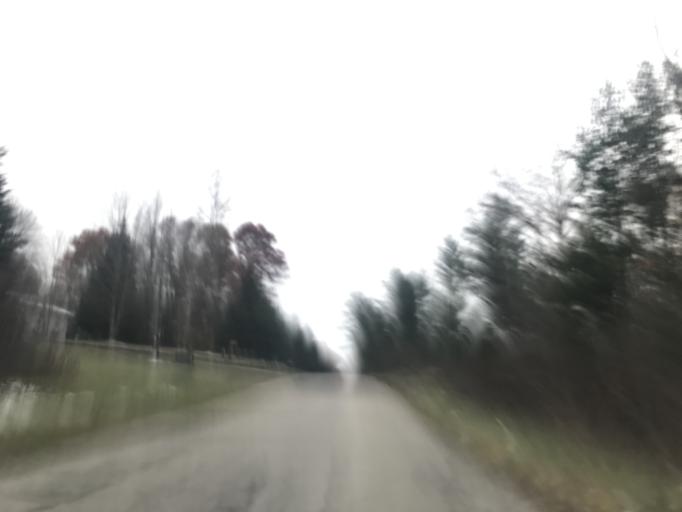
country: US
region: Wisconsin
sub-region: Marinette County
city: Peshtigo
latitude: 45.1107
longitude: -87.7500
